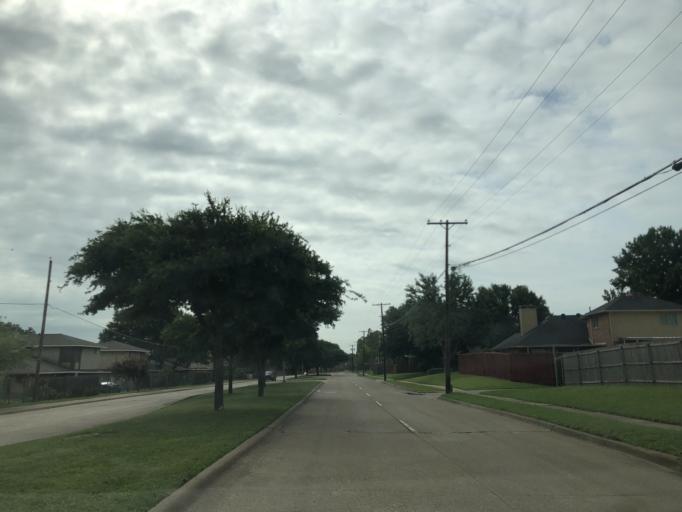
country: US
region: Texas
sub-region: Dallas County
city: Sunnyvale
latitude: 32.8320
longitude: -96.6027
